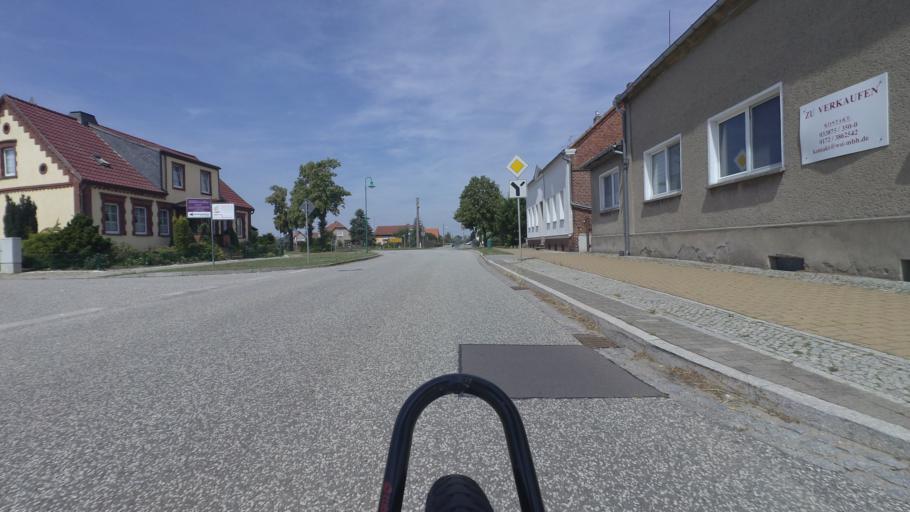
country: DE
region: Brandenburg
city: Rhinow
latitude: 52.7525
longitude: 12.3400
